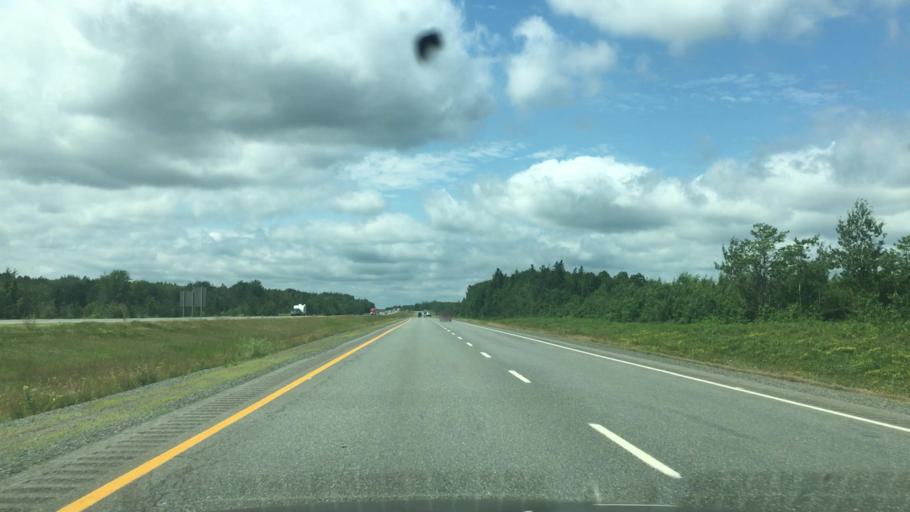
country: CA
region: Nova Scotia
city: Oxford
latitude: 45.7146
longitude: -63.9325
